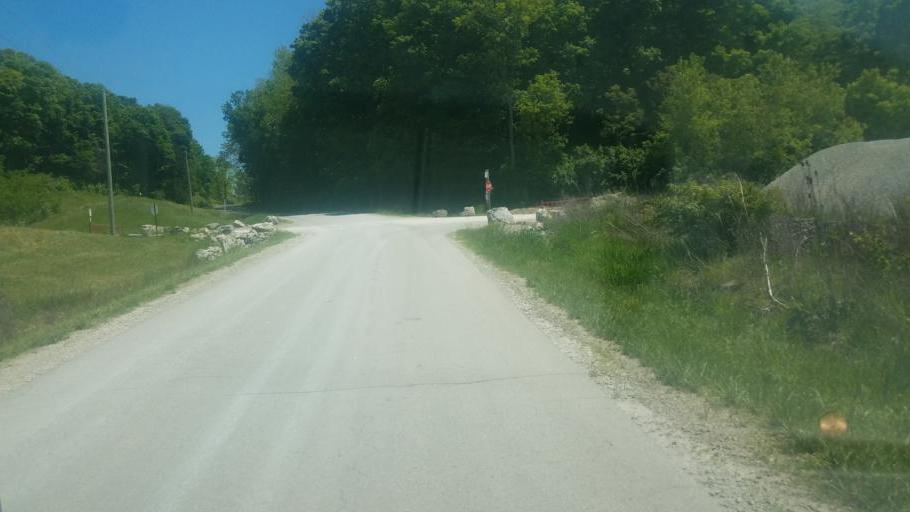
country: US
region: Ohio
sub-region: Miami County
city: Piqua
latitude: 40.2186
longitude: -84.2064
